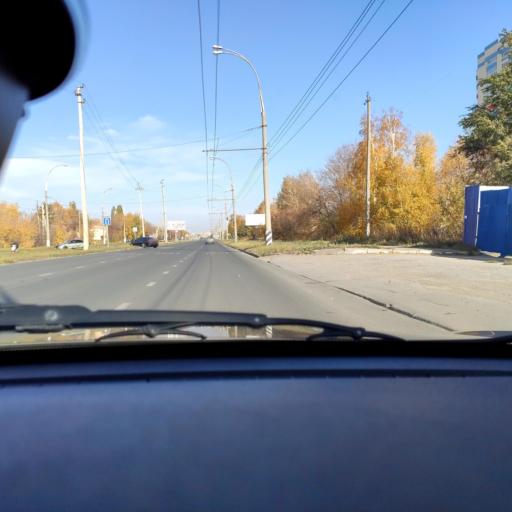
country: RU
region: Samara
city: Tol'yatti
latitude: 53.5406
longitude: 49.3004
